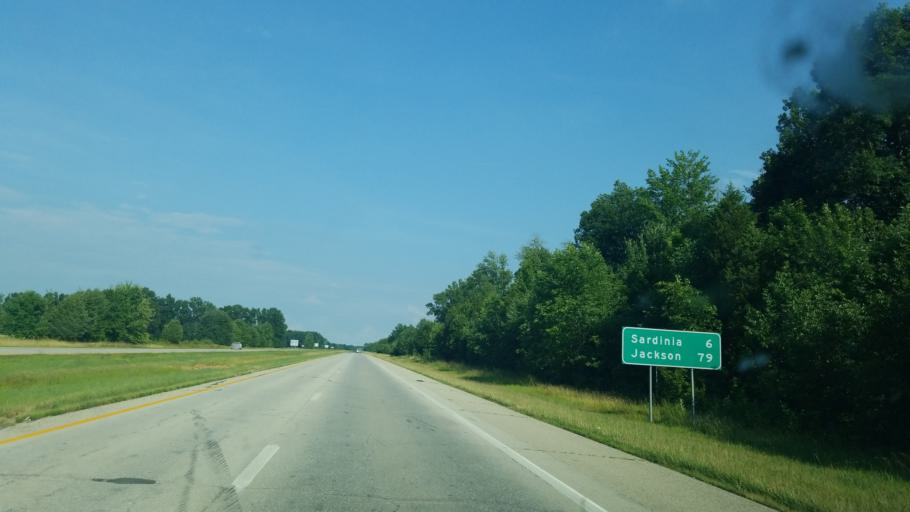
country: US
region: Ohio
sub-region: Brown County
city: Mount Orab
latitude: 39.0371
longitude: -83.9074
